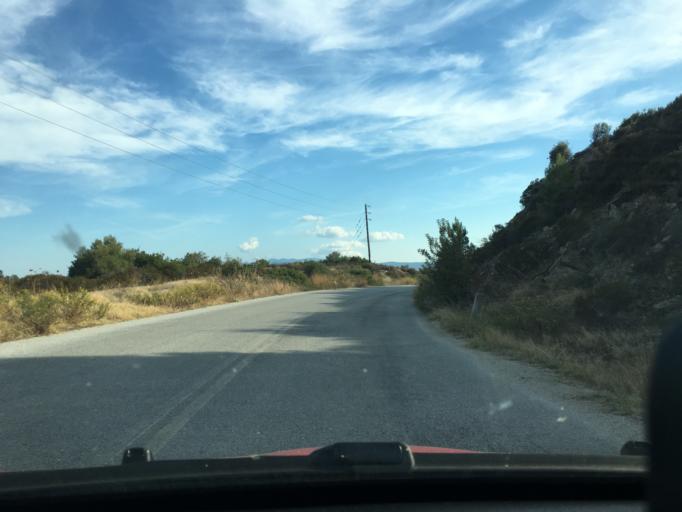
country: GR
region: Central Macedonia
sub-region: Nomos Chalkidikis
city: Agios Nikolaos
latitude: 40.3007
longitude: 23.6953
